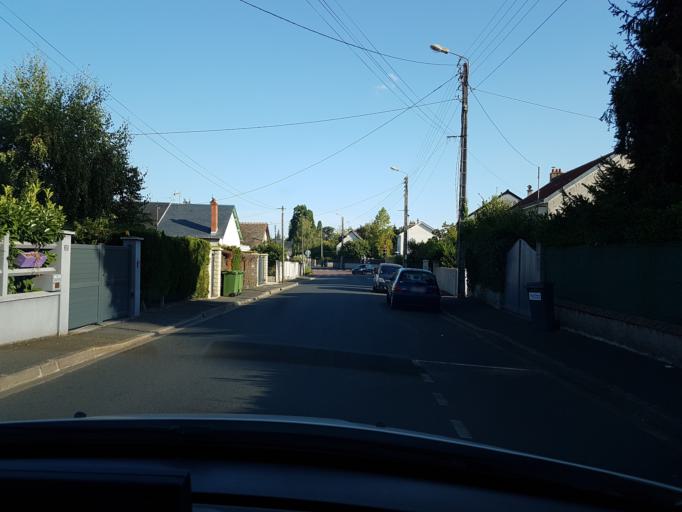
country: FR
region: Centre
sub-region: Departement d'Indre-et-Loire
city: Saint-Avertin
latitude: 47.3579
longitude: 0.7332
